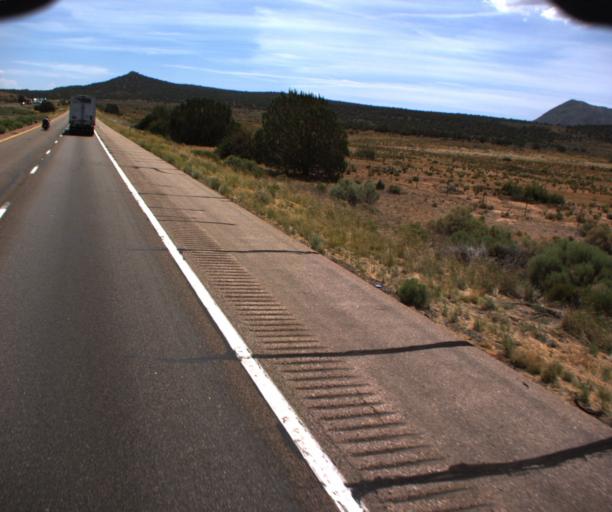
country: US
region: Arizona
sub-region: Yavapai County
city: Paulden
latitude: 35.2760
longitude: -112.7701
